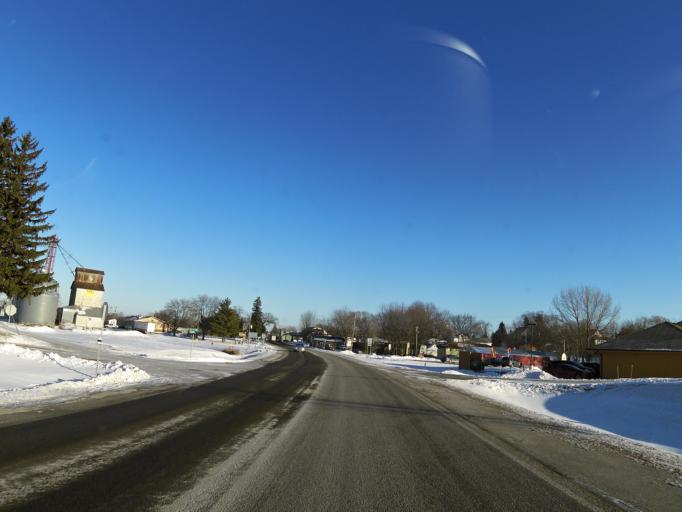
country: US
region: Minnesota
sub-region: Rice County
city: Lonsdale
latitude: 44.4807
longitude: -93.4333
